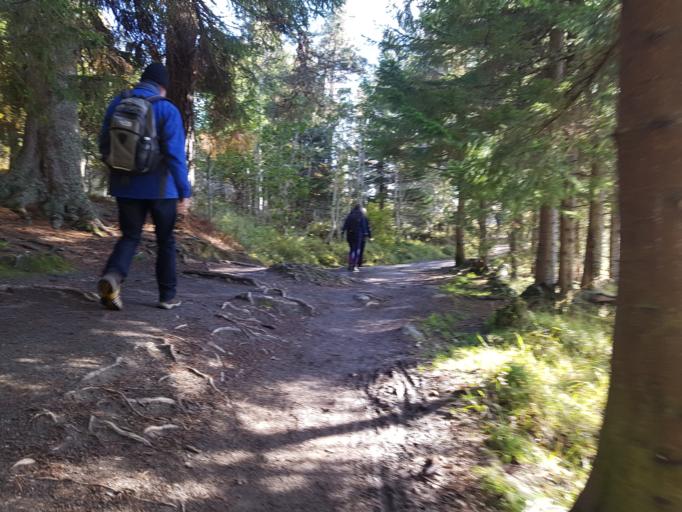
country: NO
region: Sor-Trondelag
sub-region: Trondheim
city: Trondheim
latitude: 63.4202
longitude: 10.3221
